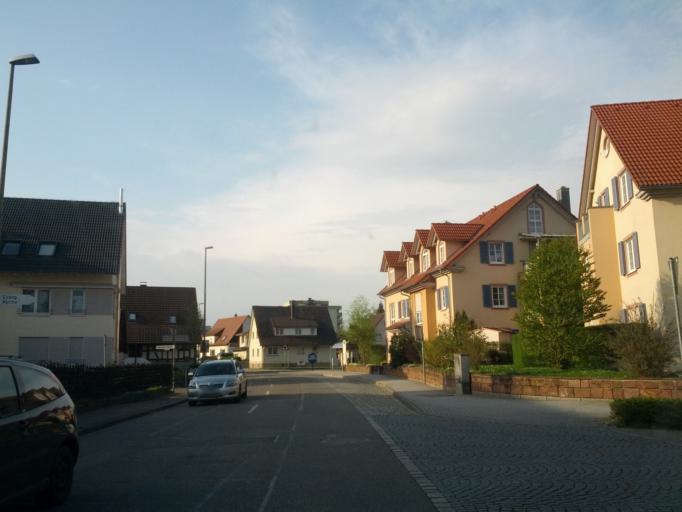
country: DE
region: Baden-Wuerttemberg
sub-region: Freiburg Region
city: Gundelfingen
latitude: 48.0453
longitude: 7.8643
